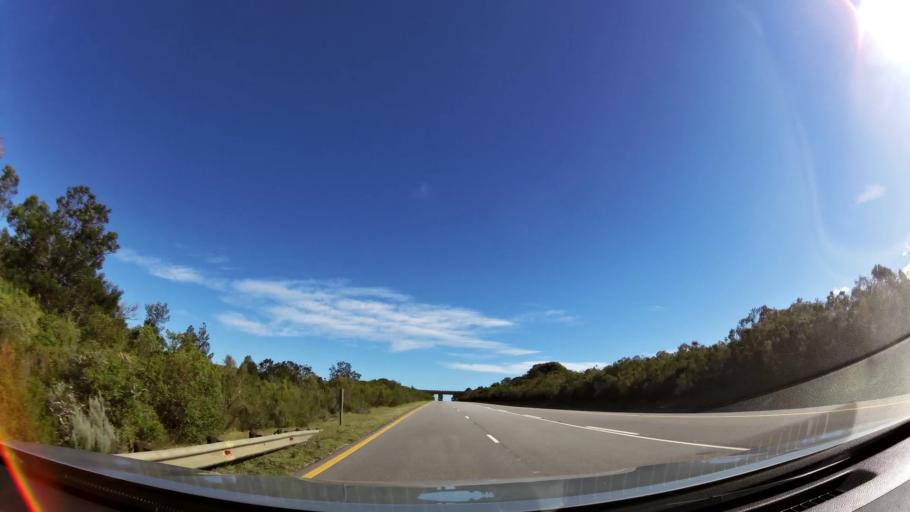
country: ZA
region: Eastern Cape
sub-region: Cacadu District Municipality
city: Kruisfontein
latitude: -34.0175
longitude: 24.6236
